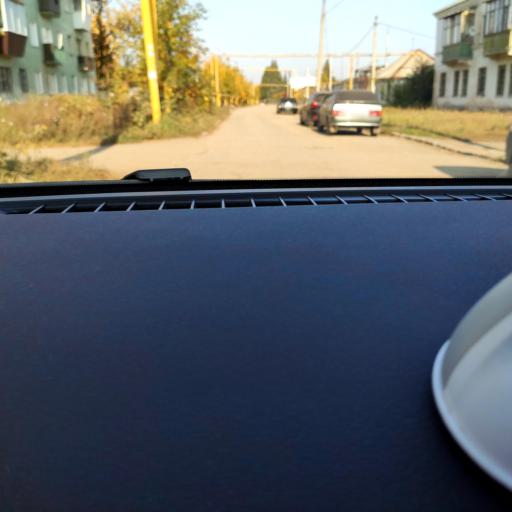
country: RU
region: Samara
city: Samara
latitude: 53.2664
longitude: 50.2380
